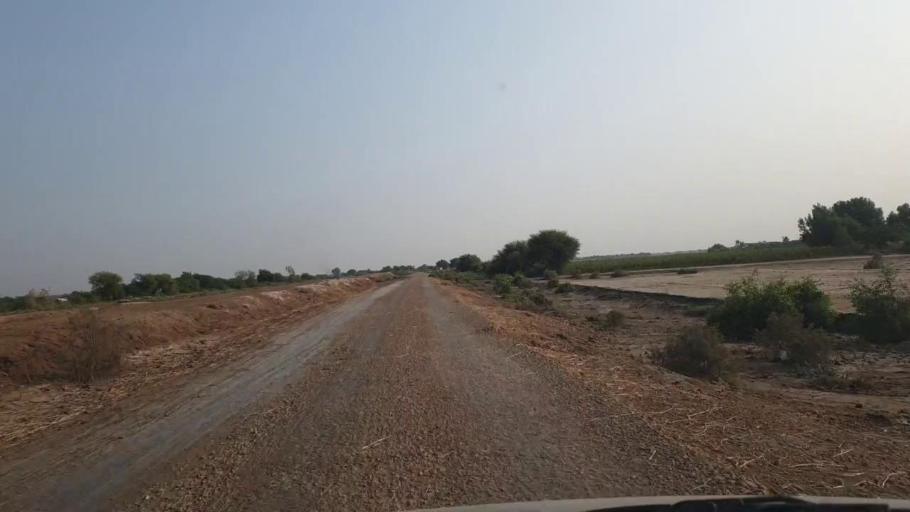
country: PK
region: Sindh
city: Matli
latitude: 25.0528
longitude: 68.7638
